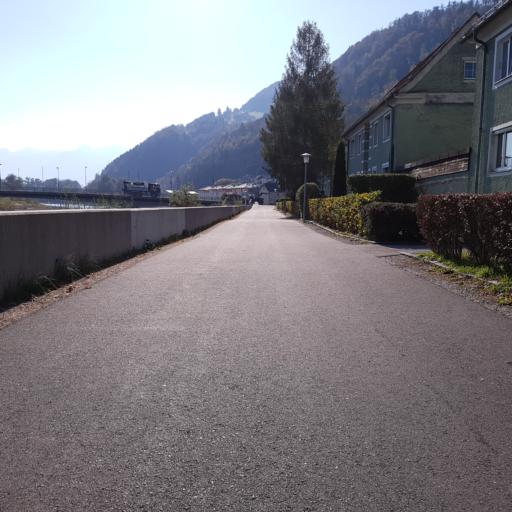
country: AT
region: Salzburg
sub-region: Politischer Bezirk Hallein
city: Hallein
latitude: 47.6781
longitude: 13.0982
